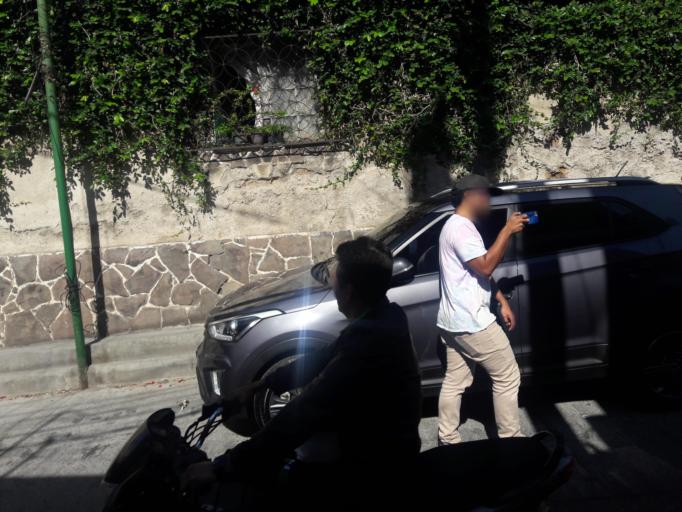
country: GT
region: Guatemala
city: Amatitlan
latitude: 14.4826
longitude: -90.6189
